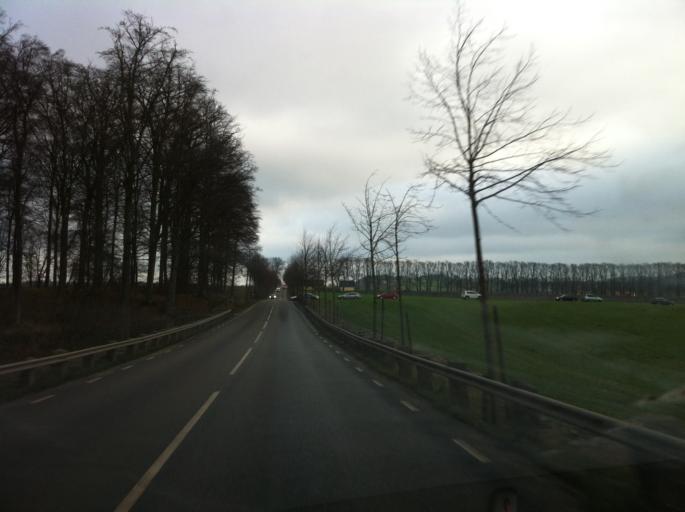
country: SE
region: Skane
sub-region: Sjobo Kommun
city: Sjoebo
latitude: 55.6921
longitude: 13.6278
